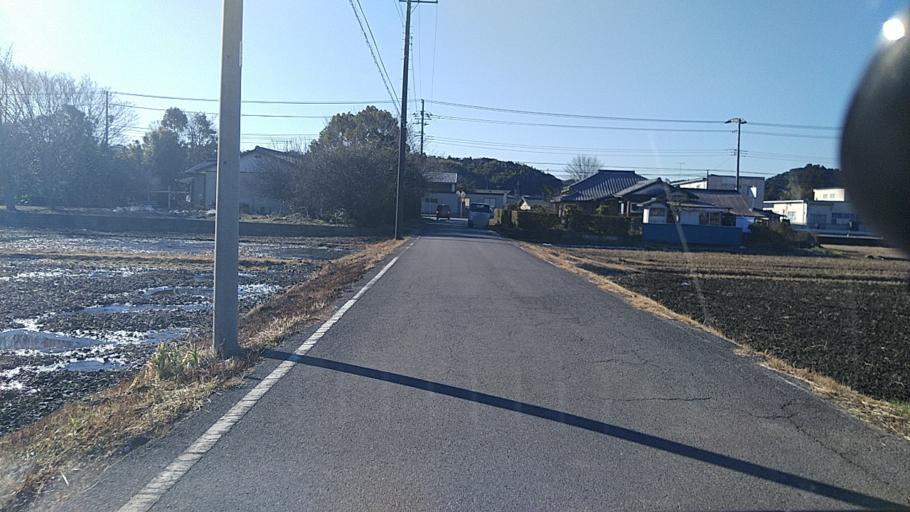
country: JP
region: Chiba
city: Kimitsu
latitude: 35.3073
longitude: 139.9527
